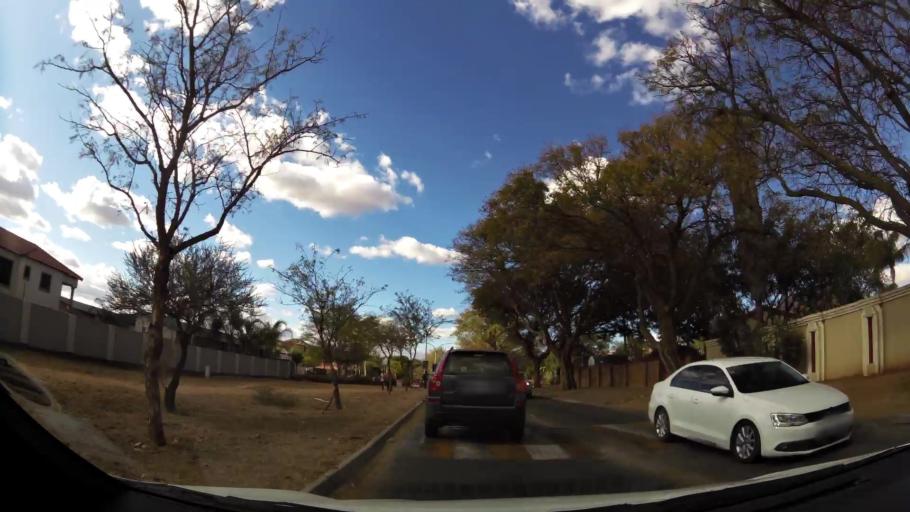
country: ZA
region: Limpopo
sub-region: Capricorn District Municipality
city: Polokwane
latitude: -23.8870
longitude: 29.4821
